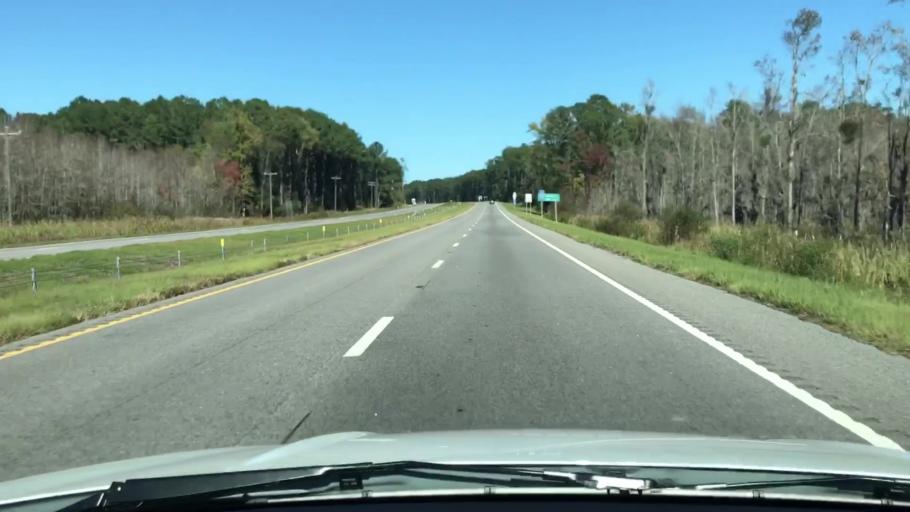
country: US
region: South Carolina
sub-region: Colleton County
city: Walterboro
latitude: 32.7091
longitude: -80.6104
